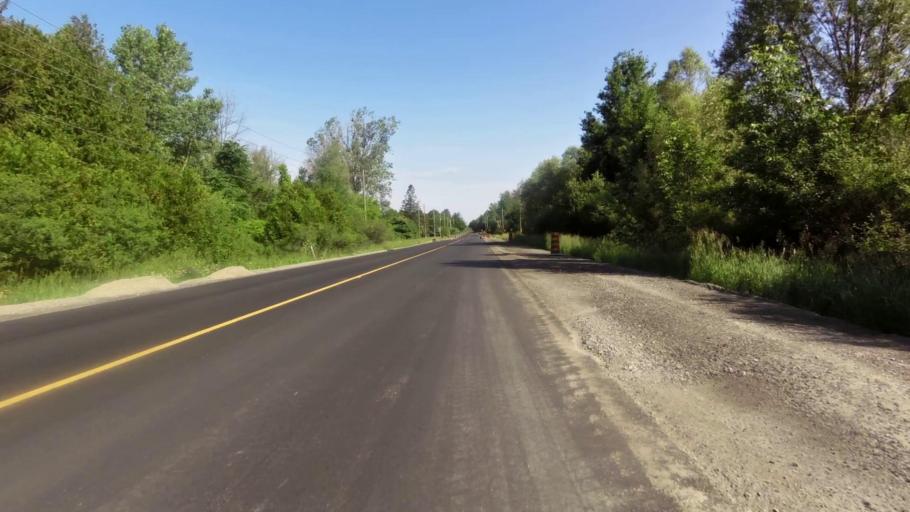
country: CA
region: Ontario
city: Ottawa
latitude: 45.2541
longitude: -75.5925
